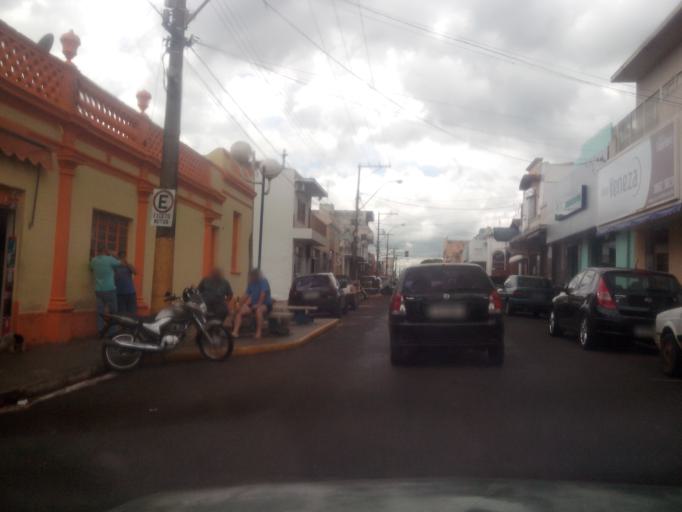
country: BR
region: Sao Paulo
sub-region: Bariri
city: Bariri
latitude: -22.0751
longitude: -48.7396
